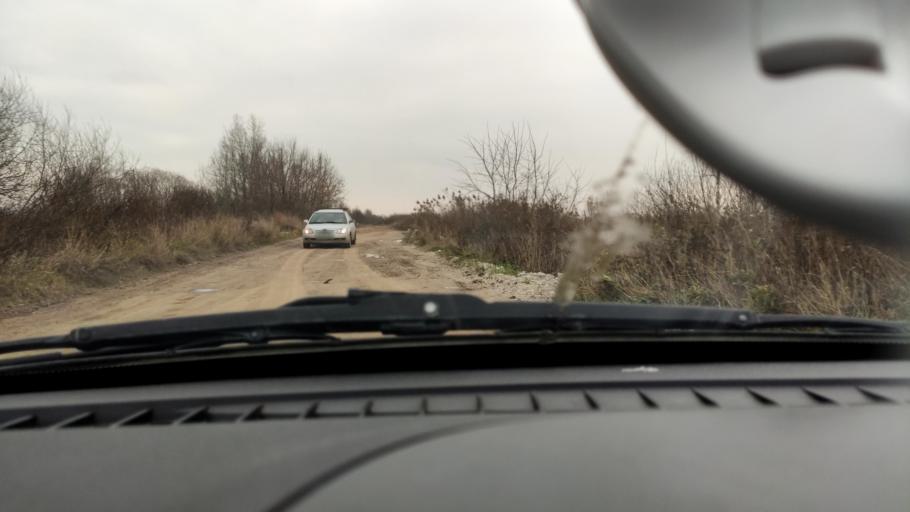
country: RU
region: Perm
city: Kondratovo
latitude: 57.9882
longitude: 56.0787
